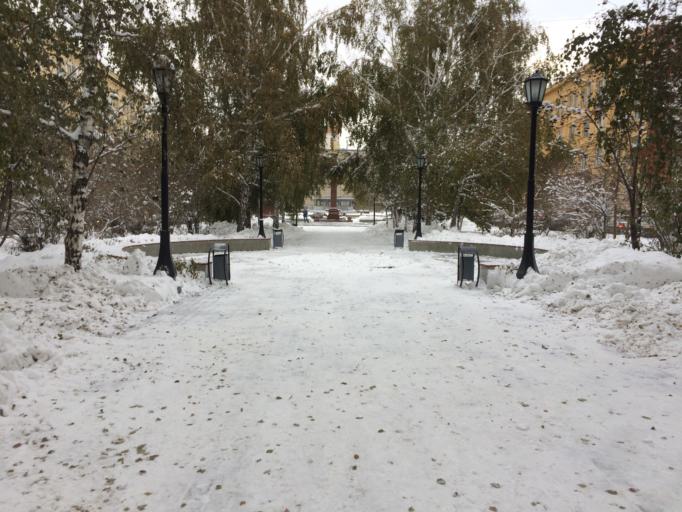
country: RU
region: Novosibirsk
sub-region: Novosibirskiy Rayon
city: Novosibirsk
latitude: 55.0151
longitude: 82.9445
